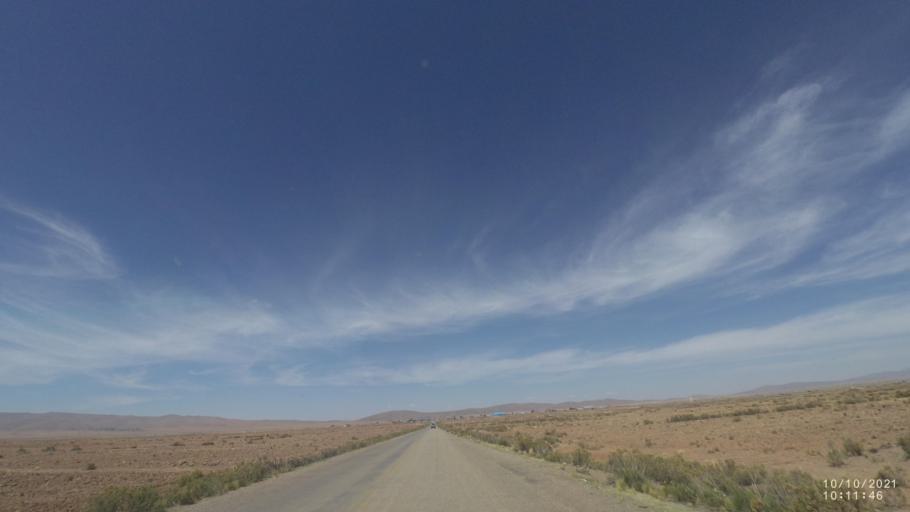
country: BO
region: La Paz
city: Eucaliptus
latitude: -17.4273
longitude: -67.5076
